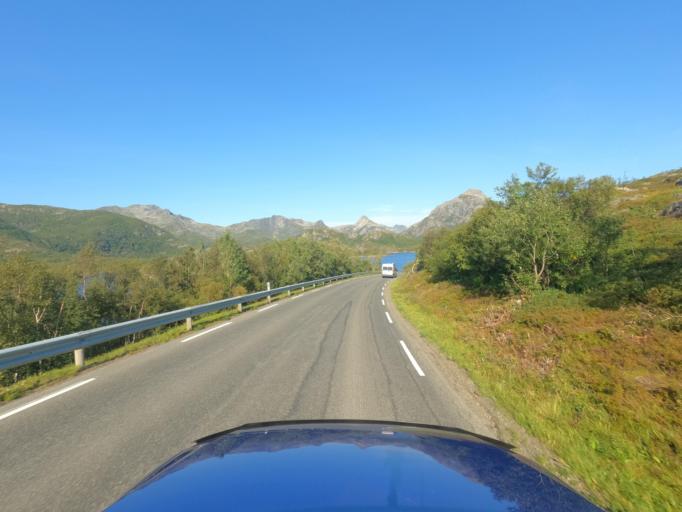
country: NO
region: Nordland
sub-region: Vagan
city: Svolvaer
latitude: 68.2587
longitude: 14.6574
